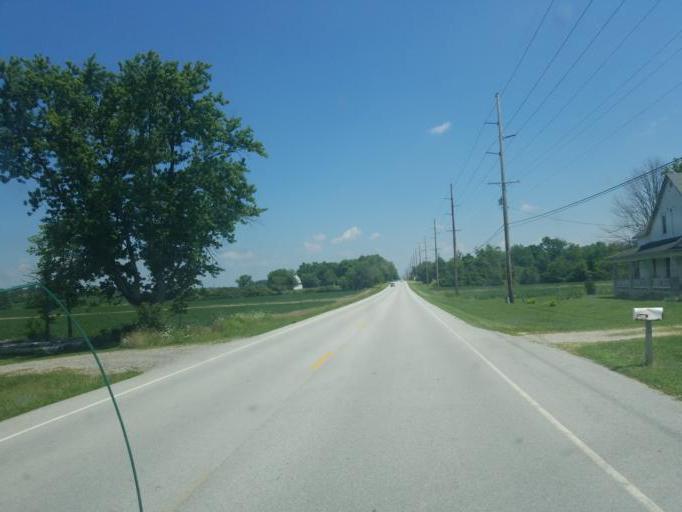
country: US
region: Ohio
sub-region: Auglaize County
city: Saint Marys
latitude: 40.5544
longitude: -84.3105
